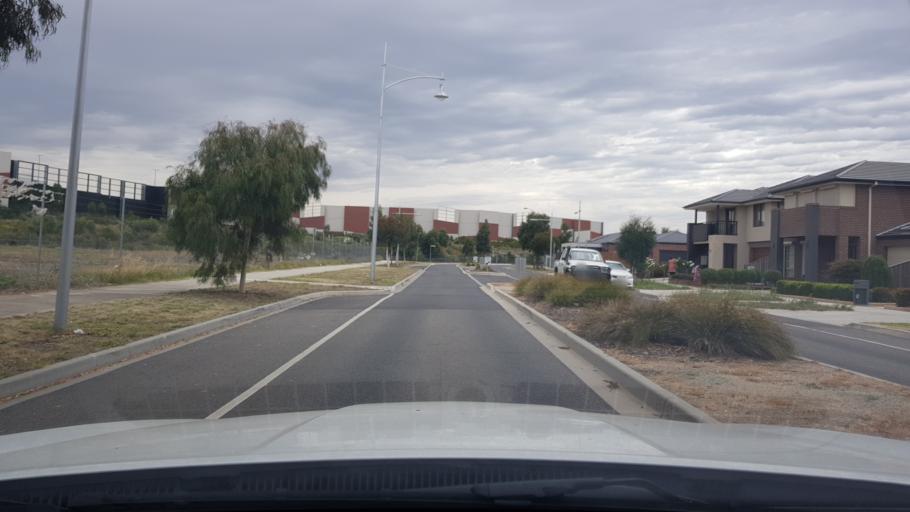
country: AU
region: Victoria
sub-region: Whittlesea
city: Lalor
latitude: -37.6593
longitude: 144.9969
